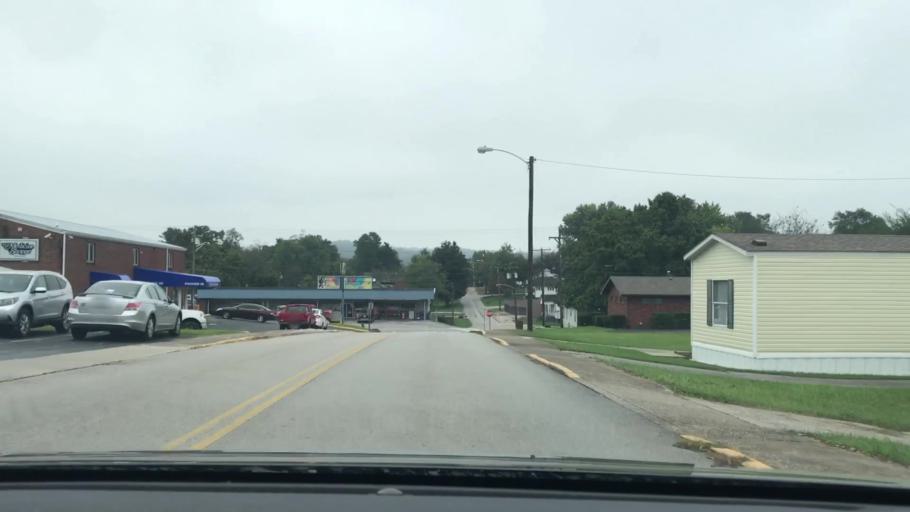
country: US
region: Kentucky
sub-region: Pulaski County
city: Somerset
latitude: 37.0968
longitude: -84.5926
